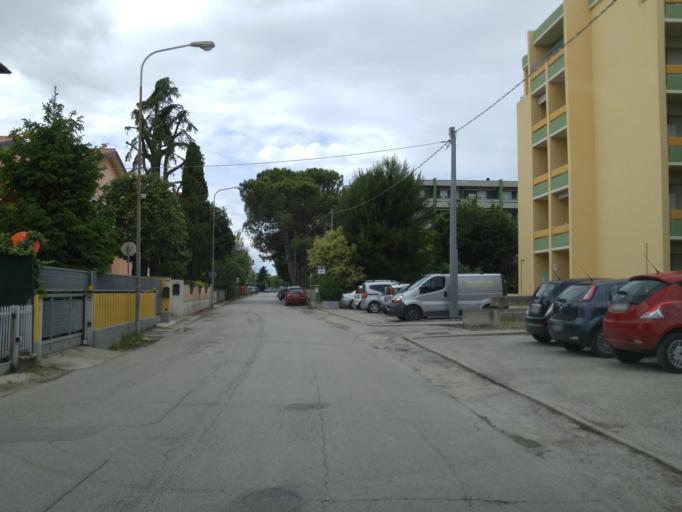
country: IT
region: The Marches
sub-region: Provincia di Pesaro e Urbino
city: Fano
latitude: 43.8329
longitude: 13.0288
